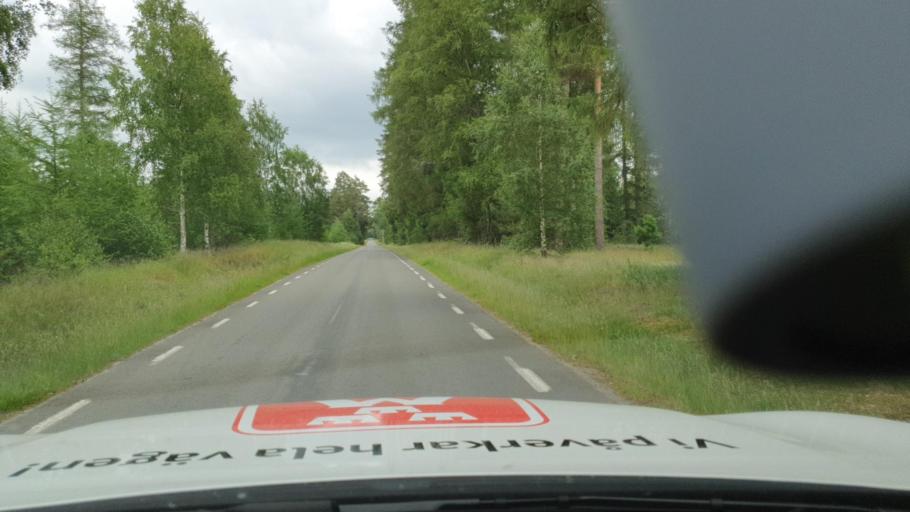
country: SE
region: Vaestra Goetaland
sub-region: Tidaholms Kommun
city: Olofstorp
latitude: 58.1926
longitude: 14.1027
